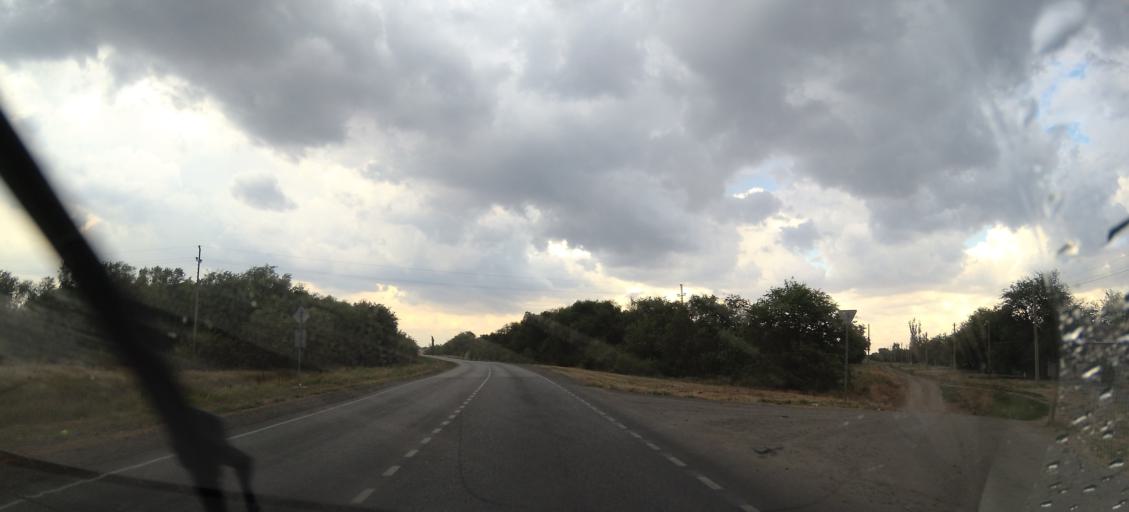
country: RU
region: Rostov
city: Orlovskiy
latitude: 46.8863
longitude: 42.0428
